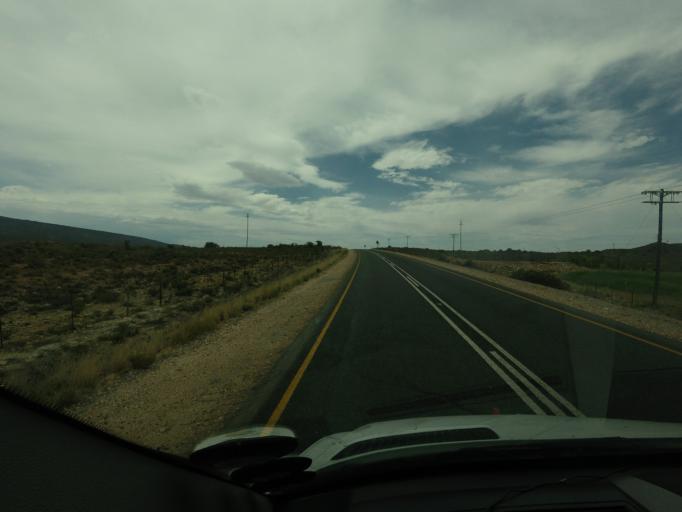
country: ZA
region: Western Cape
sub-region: Overberg District Municipality
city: Swellendam
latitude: -33.8479
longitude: 20.8588
